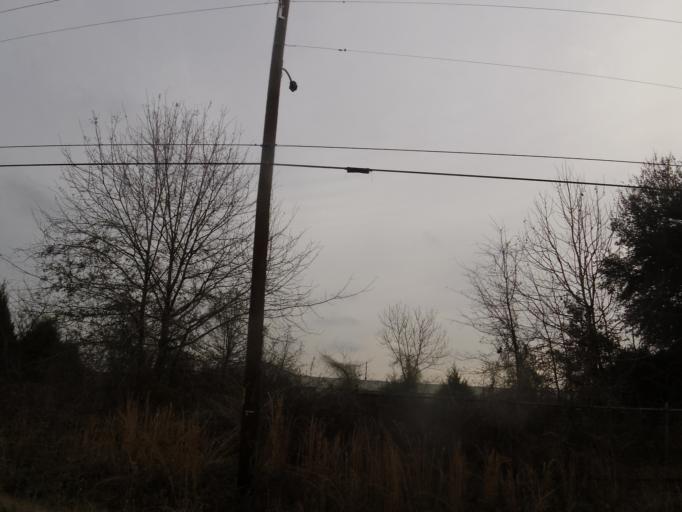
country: US
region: Alabama
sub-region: Montgomery County
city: Montgomery
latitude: 32.3873
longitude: -86.3121
